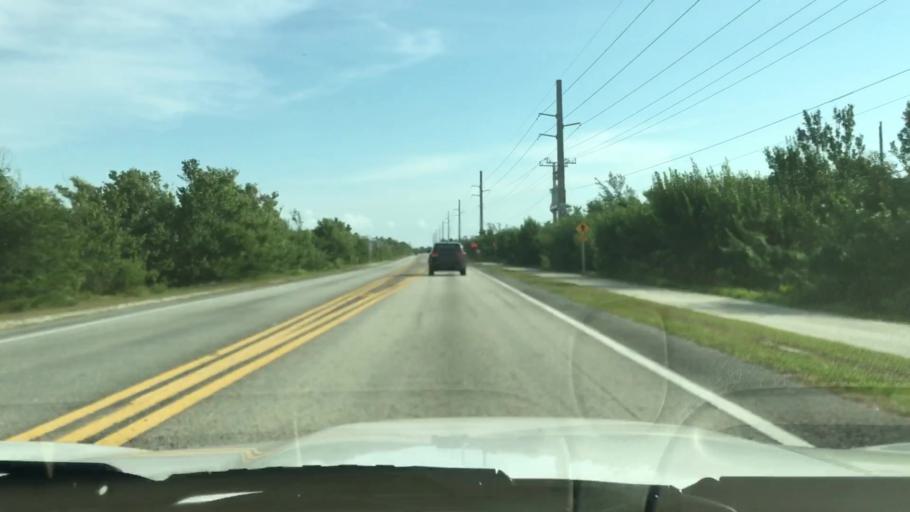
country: US
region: Florida
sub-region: Monroe County
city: Cudjoe Key
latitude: 24.6636
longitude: -81.5100
